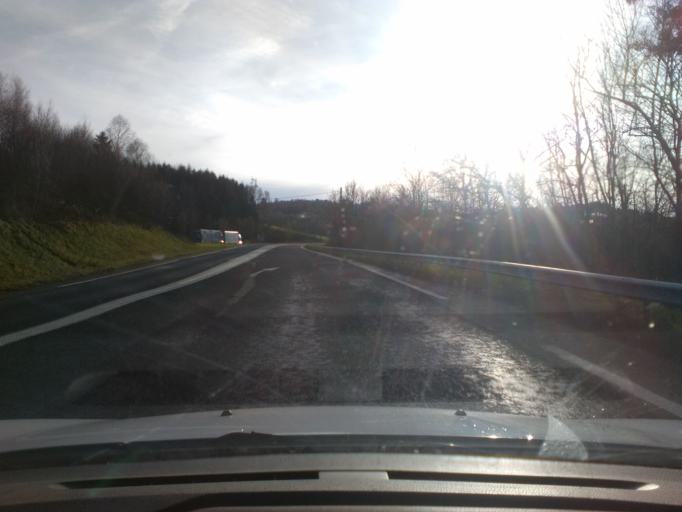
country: FR
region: Lorraine
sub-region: Departement des Vosges
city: Anould
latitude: 48.1764
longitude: 6.9287
